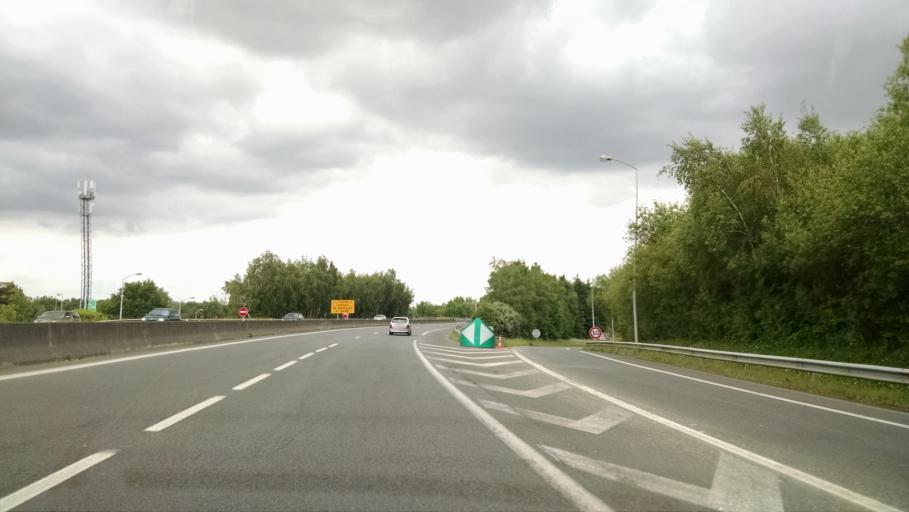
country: FR
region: Pays de la Loire
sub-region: Departement de la Loire-Atlantique
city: Basse-Goulaine
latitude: 47.2103
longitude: -1.4851
